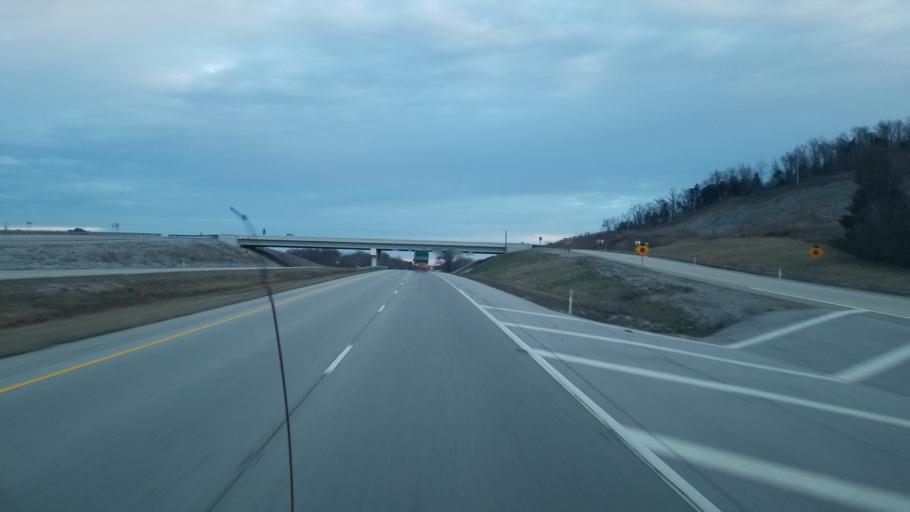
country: US
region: Tennessee
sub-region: White County
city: Sparta
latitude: 35.9889
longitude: -85.5004
